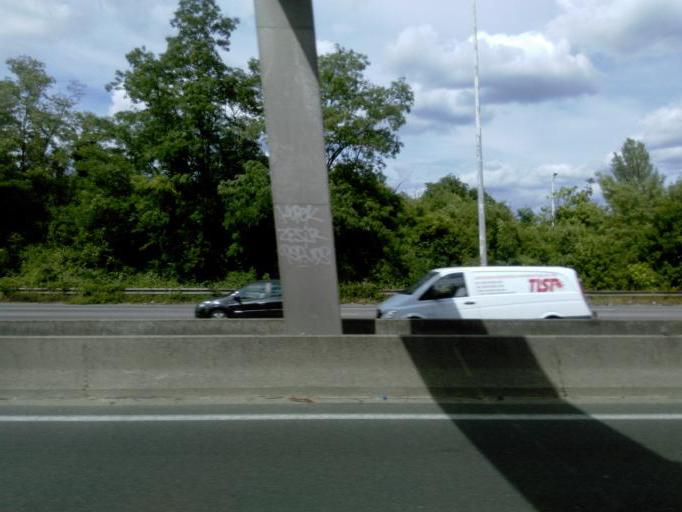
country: FR
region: Ile-de-France
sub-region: Departement du Val-d'Oise
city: Sannois
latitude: 48.9616
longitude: 2.2681
